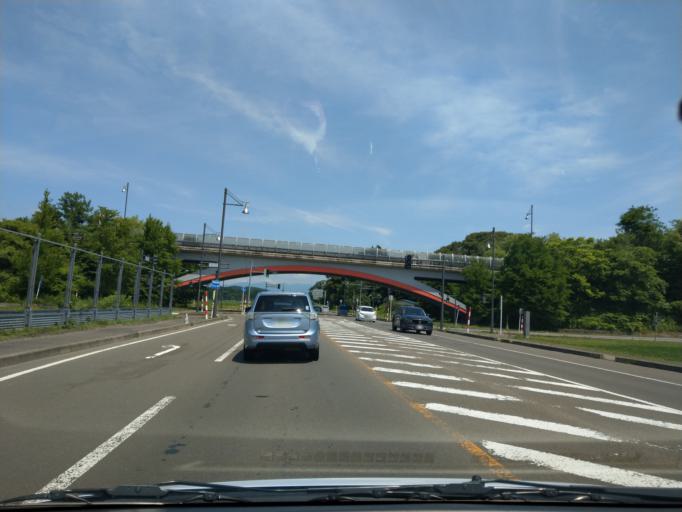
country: JP
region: Akita
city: Takanosu
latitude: 40.1874
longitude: 140.4005
